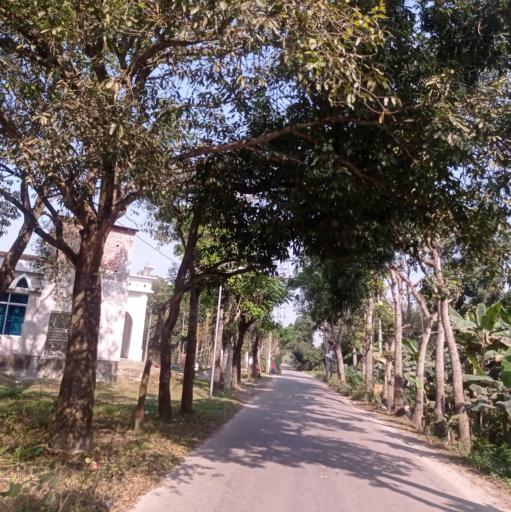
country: BD
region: Dhaka
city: Narsingdi
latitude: 24.0304
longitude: 90.6731
